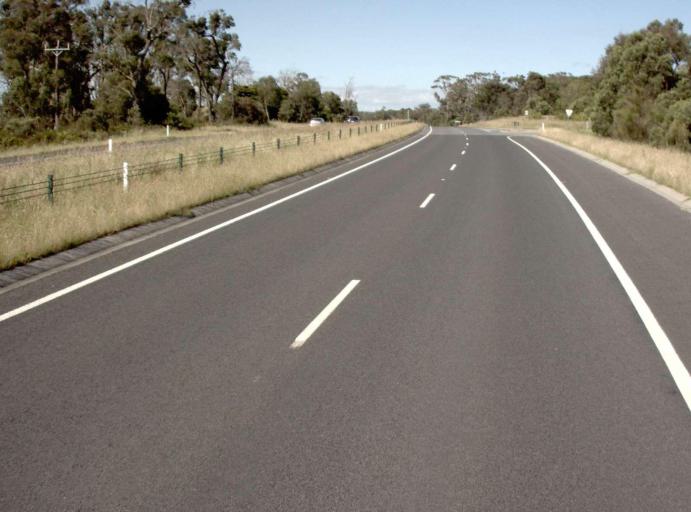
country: AU
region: Victoria
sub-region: Bass Coast
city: North Wonthaggi
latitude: -38.4235
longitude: 145.5156
